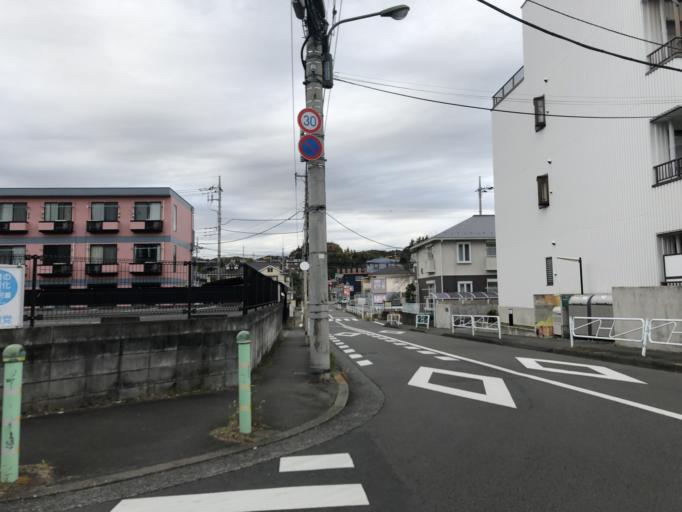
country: JP
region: Tokyo
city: Hino
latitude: 35.6255
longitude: 139.3822
